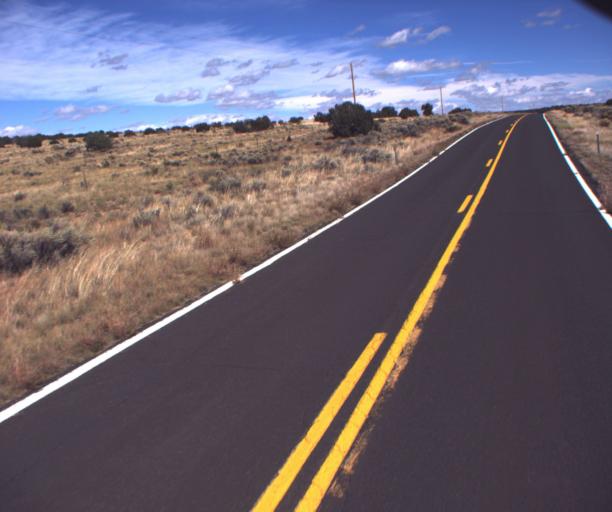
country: US
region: Arizona
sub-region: Apache County
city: Houck
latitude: 34.9463
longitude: -109.1735
